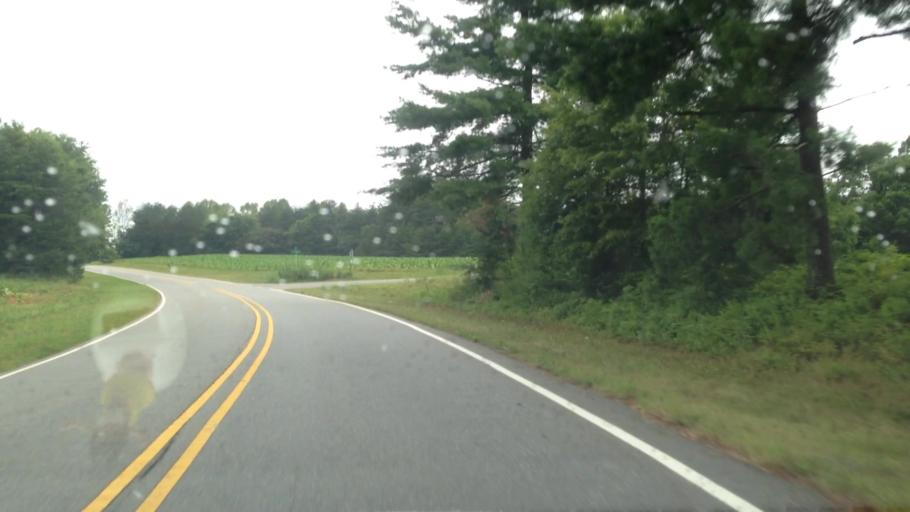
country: US
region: North Carolina
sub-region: Rockingham County
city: Mayodan
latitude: 36.4044
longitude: -80.0427
